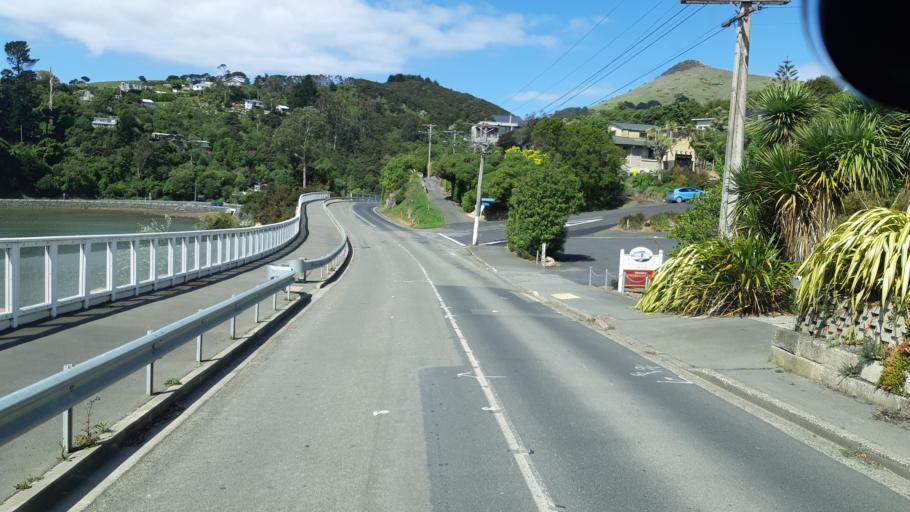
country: NZ
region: Otago
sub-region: Dunedin City
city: Portobello
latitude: -45.8463
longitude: 170.6289
